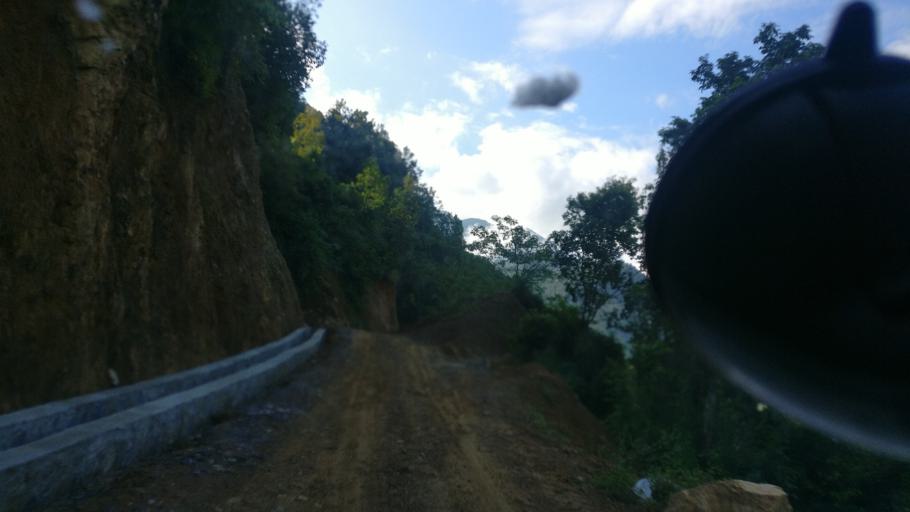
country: NP
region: Western Region
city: Baglung
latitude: 28.1579
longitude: 83.6538
